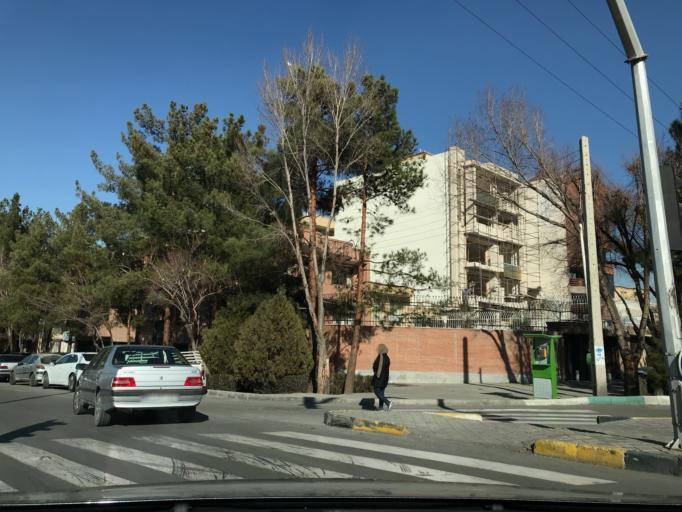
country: IR
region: Isfahan
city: Isfahan
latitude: 32.6144
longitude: 51.6739
